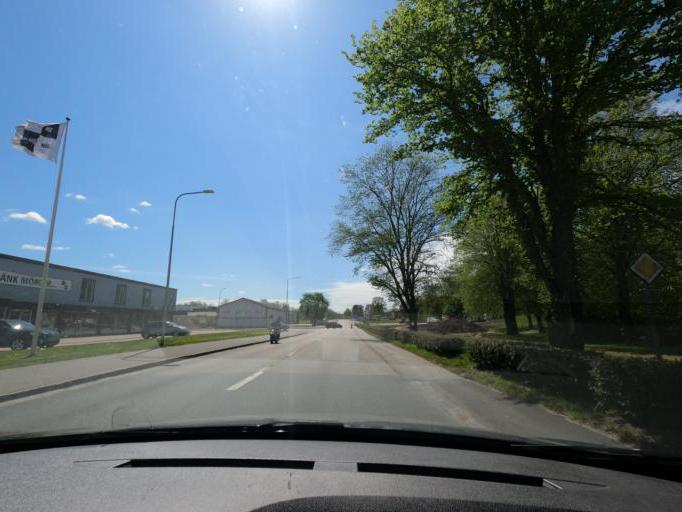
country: SE
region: Joenkoeping
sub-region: Varnamo Kommun
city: Bredaryd
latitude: 57.1747
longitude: 13.7406
